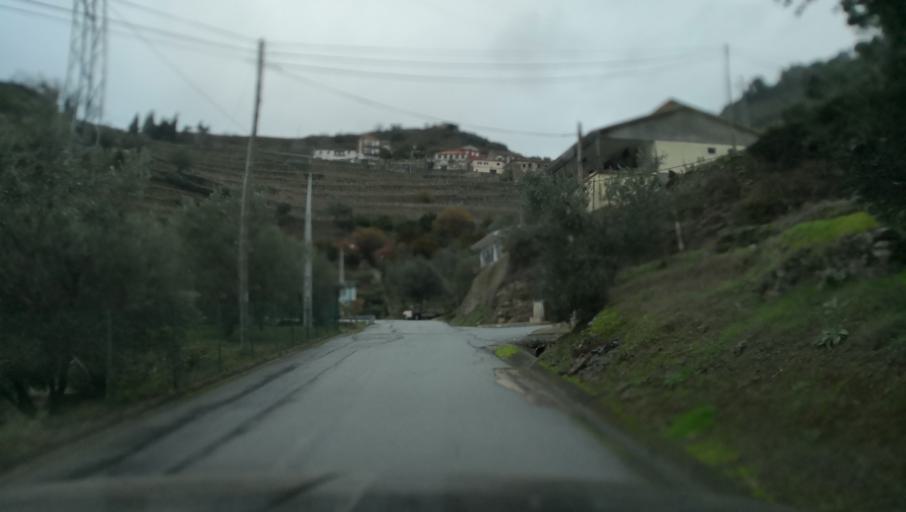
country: PT
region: Vila Real
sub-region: Santa Marta de Penaguiao
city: Santa Marta de Penaguiao
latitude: 41.2034
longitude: -7.7500
